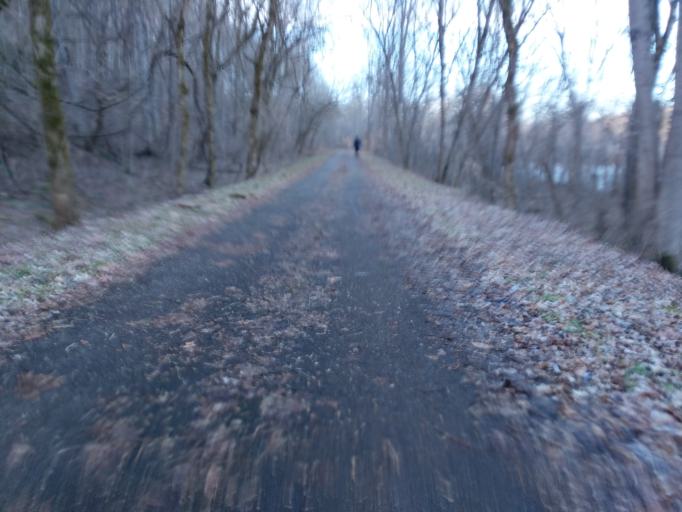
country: US
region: Ohio
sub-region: Athens County
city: Athens
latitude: 39.3535
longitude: -82.1062
